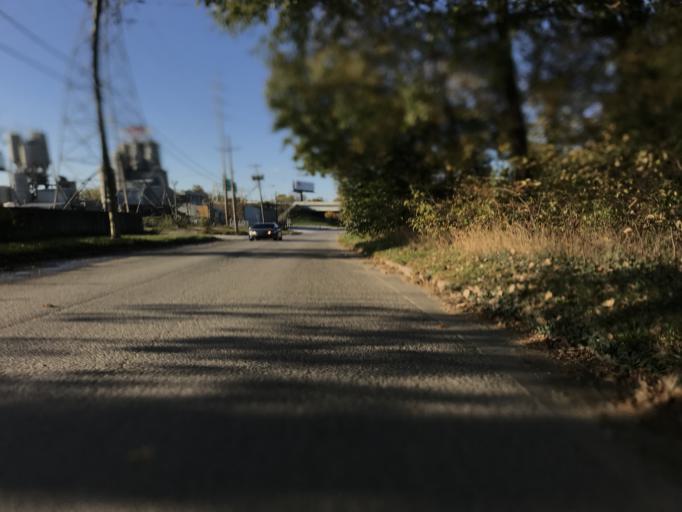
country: US
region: Indiana
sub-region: Clark County
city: Jeffersonville
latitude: 38.2607
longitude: -85.7232
